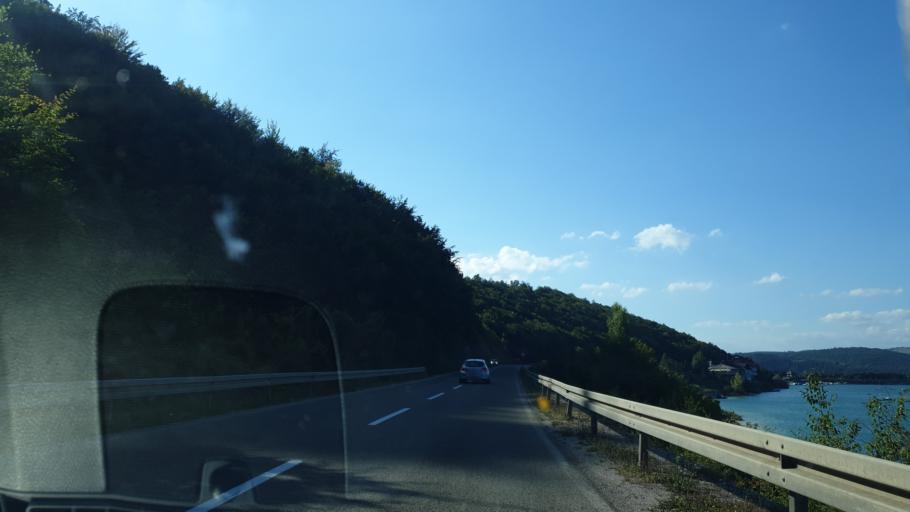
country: RS
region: Central Serbia
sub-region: Zlatiborski Okrug
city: Nova Varos
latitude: 43.5035
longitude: 19.8171
